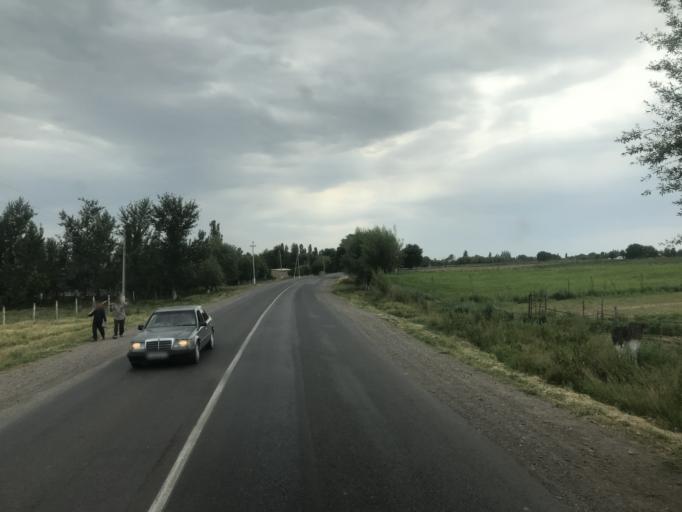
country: KZ
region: Ongtustik Qazaqstan
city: Saryaghash
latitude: 41.3785
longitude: 69.0154
